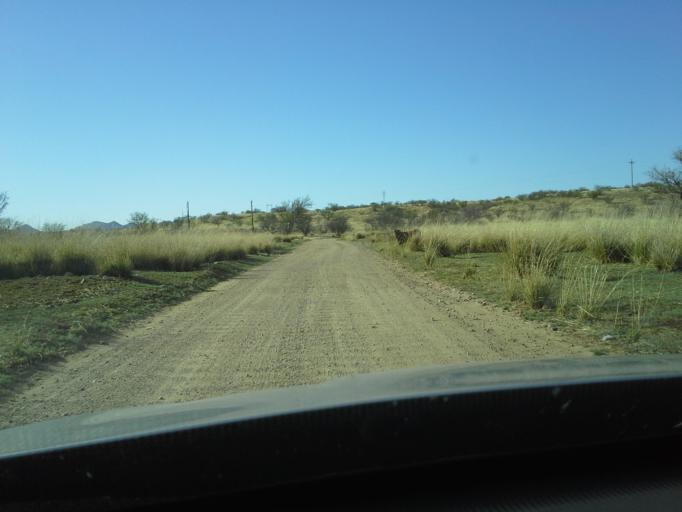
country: US
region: Arizona
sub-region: Pima County
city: Corona de Tucson
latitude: 31.7363
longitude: -110.6799
